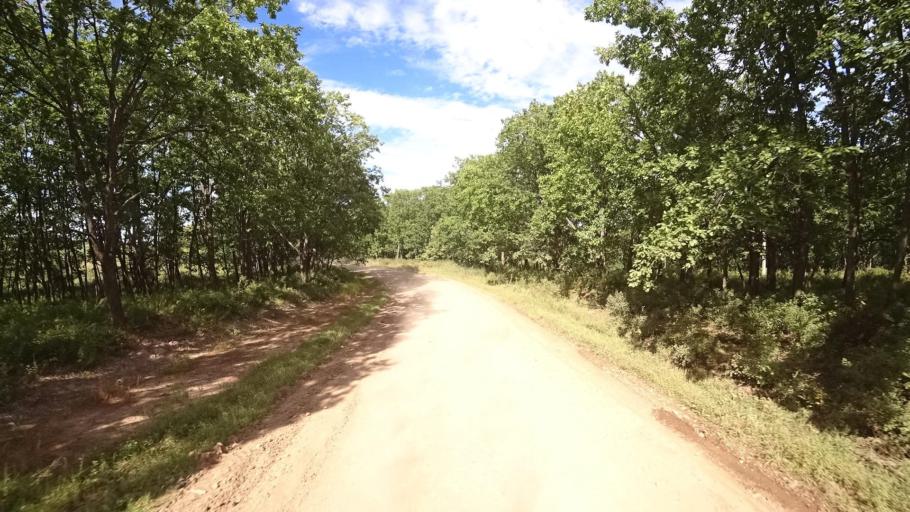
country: RU
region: Primorskiy
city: Yakovlevka
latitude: 44.4035
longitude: 133.5659
